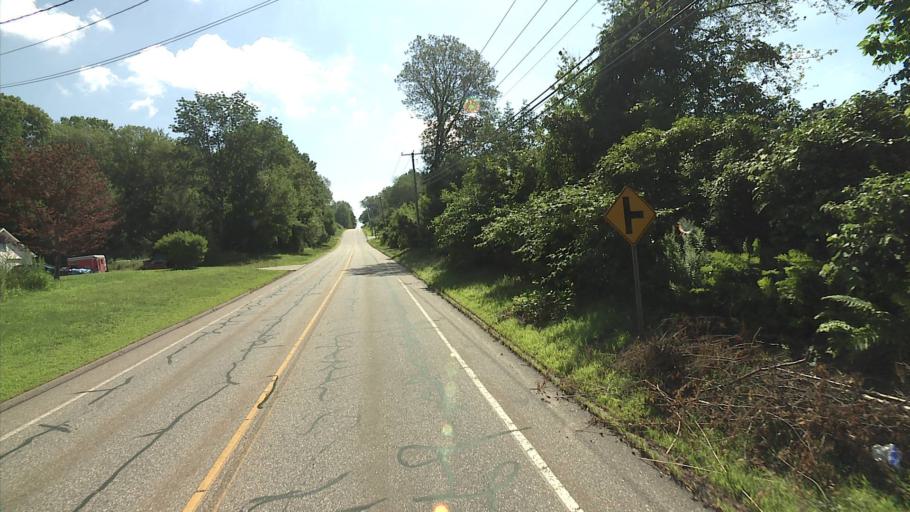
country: US
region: Connecticut
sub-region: Windham County
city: Windham
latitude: 41.6986
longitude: -72.0758
